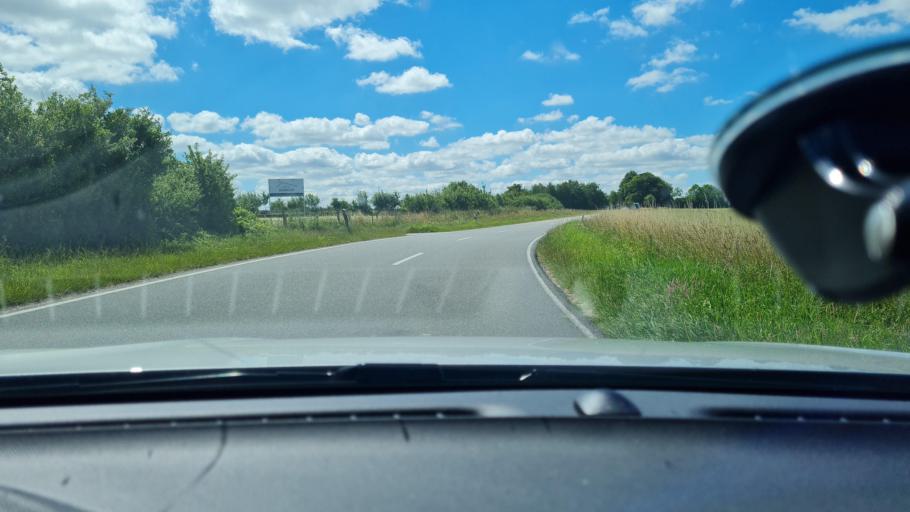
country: DE
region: Schleswig-Holstein
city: Winnemark
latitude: 54.6004
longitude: 9.9165
